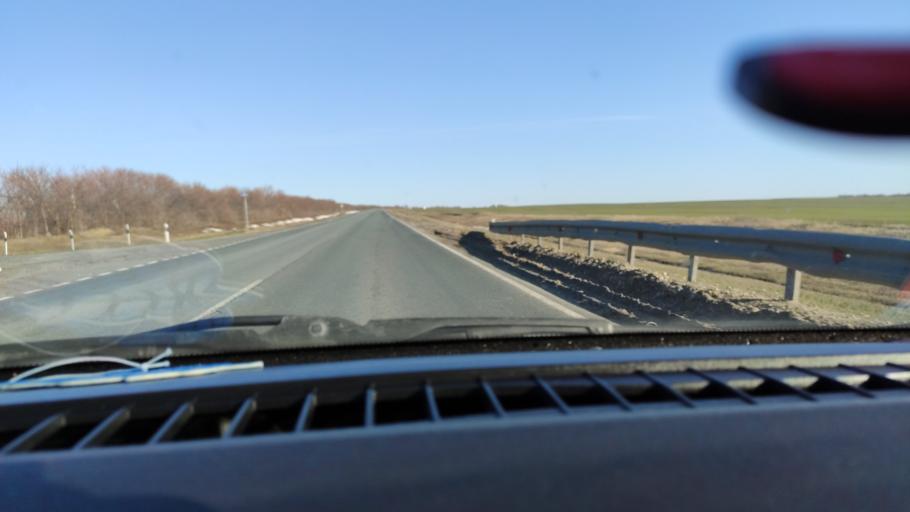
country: RU
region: Saratov
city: Dukhovnitskoye
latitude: 52.7596
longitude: 48.2425
